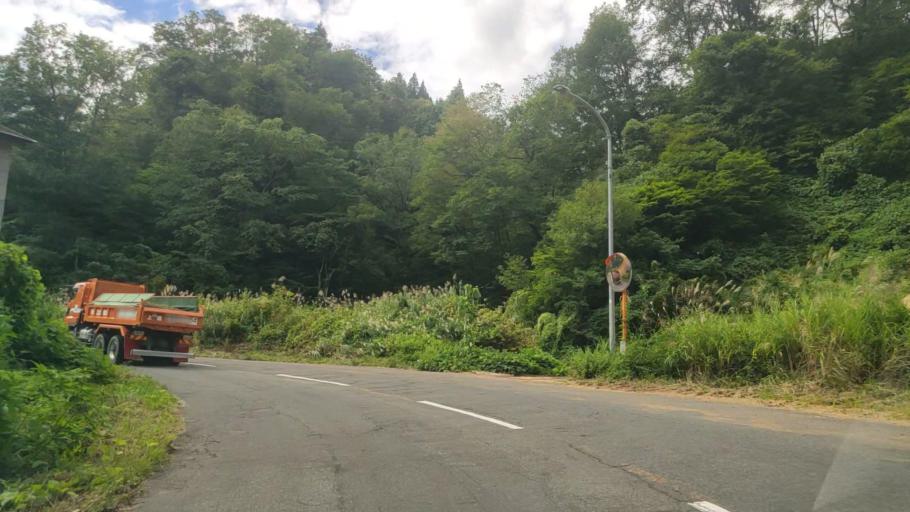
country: JP
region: Nagano
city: Iiyama
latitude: 36.8899
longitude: 138.3232
